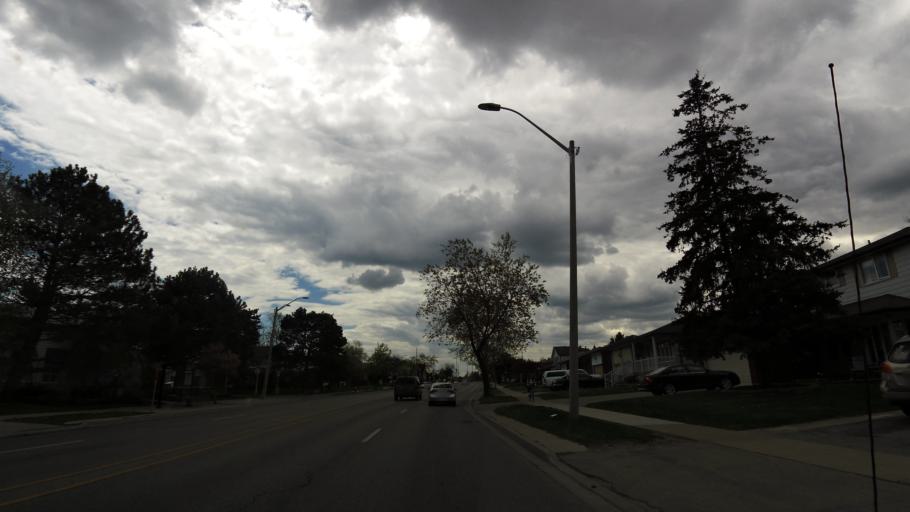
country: CA
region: Ontario
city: Etobicoke
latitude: 43.6090
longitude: -79.6018
